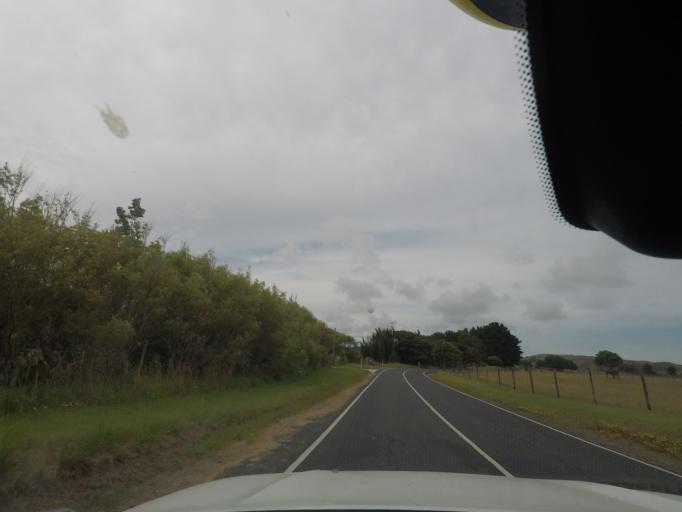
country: NZ
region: Auckland
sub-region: Auckland
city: Parakai
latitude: -36.5136
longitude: 174.2482
